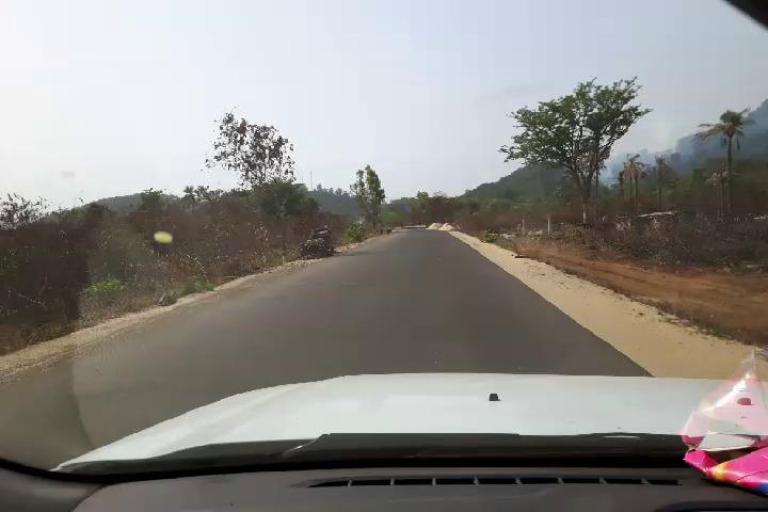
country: SL
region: Western Area
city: Waterloo
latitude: 8.2546
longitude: -13.1567
